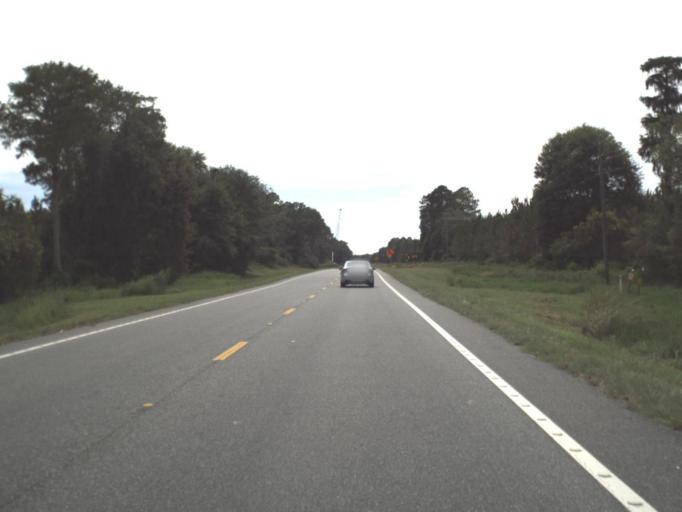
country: US
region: Florida
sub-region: Taylor County
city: Perry
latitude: 30.0992
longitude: -83.4642
